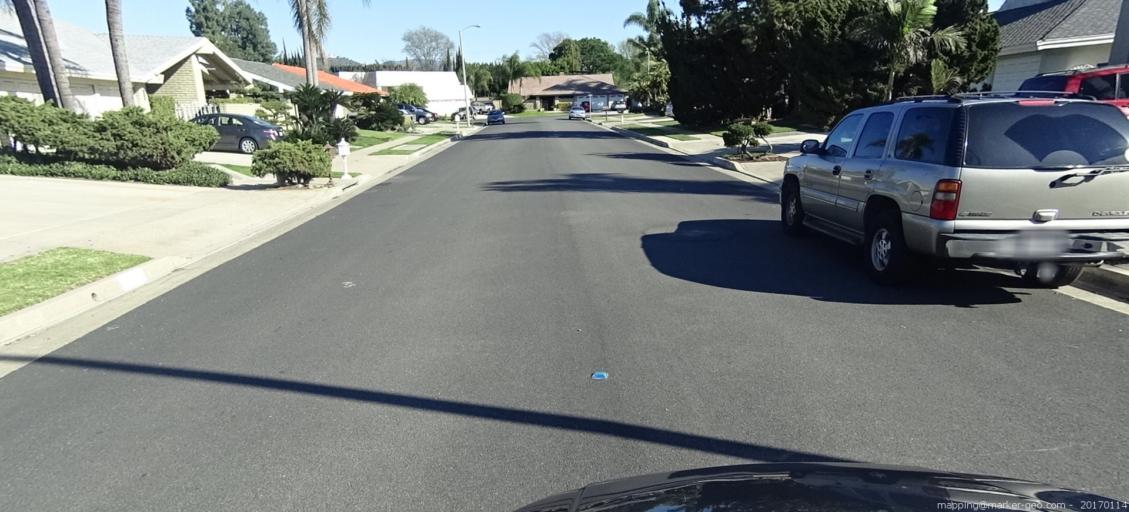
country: US
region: California
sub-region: Orange County
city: North Tustin
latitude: 33.7729
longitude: -117.8176
